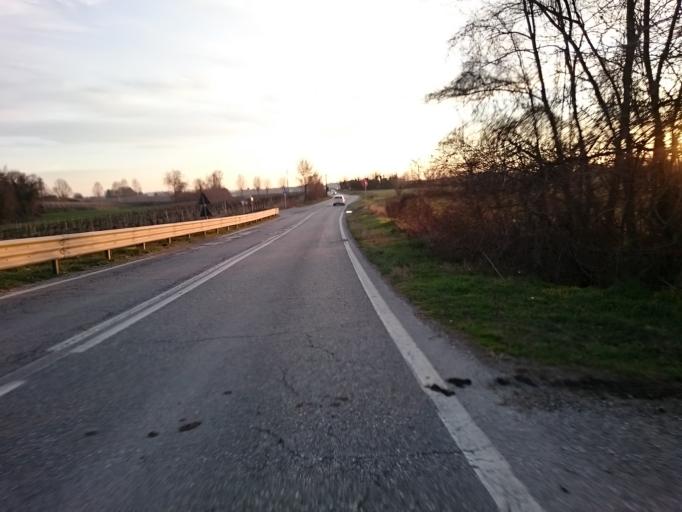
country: IT
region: Veneto
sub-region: Provincia di Verona
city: Castelnuovo del Garda
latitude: 45.4256
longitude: 10.7552
